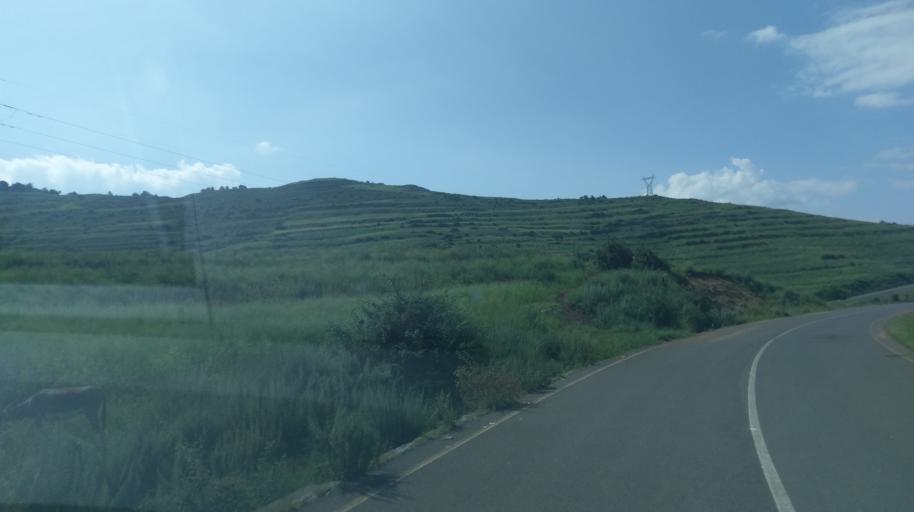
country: LS
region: Thaba-Tseka
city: Thaba-Tseka
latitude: -29.1257
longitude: 28.4920
